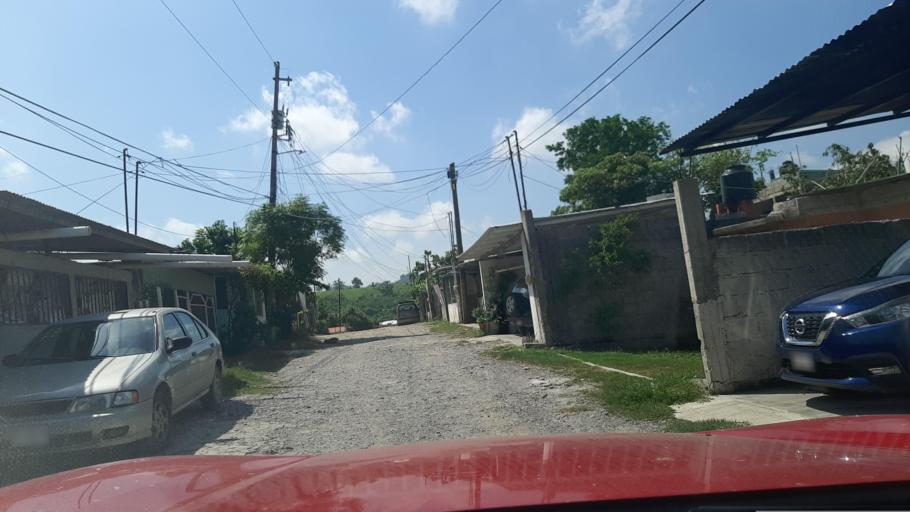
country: MX
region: Veracruz
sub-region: Poza Rica de Hidalgo
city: El Mollejon
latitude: 20.5431
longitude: -97.4095
